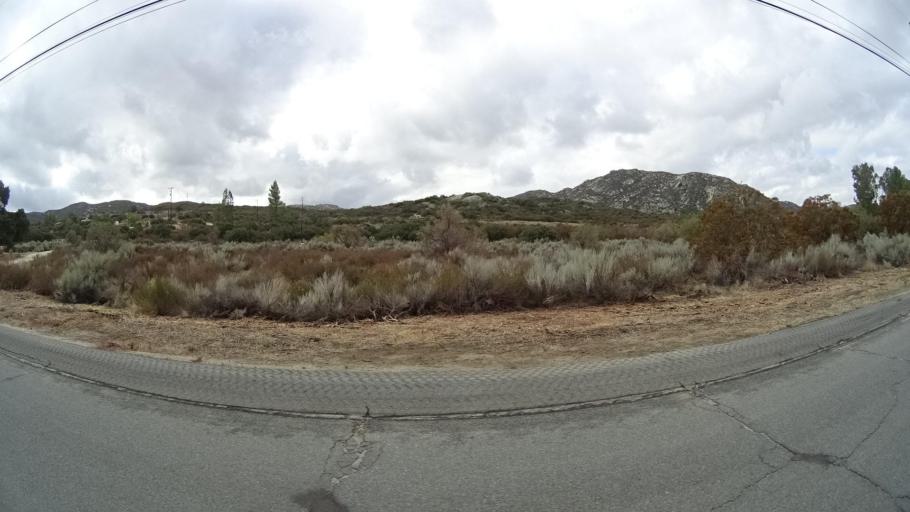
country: US
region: California
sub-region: San Diego County
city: Campo
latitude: 32.6300
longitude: -116.4222
